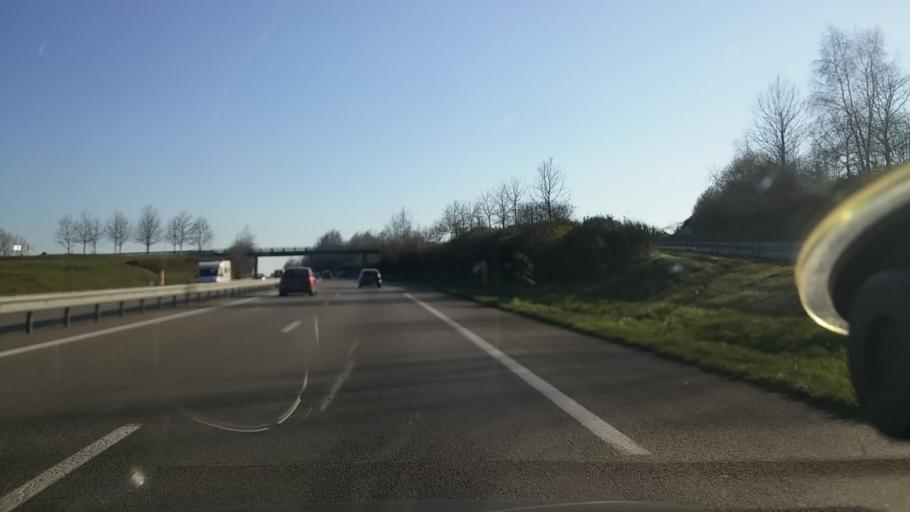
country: FR
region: Limousin
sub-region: Departement de la Haute-Vienne
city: Saint-Sulpice-les-Feuilles
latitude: 46.3567
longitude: 1.4279
